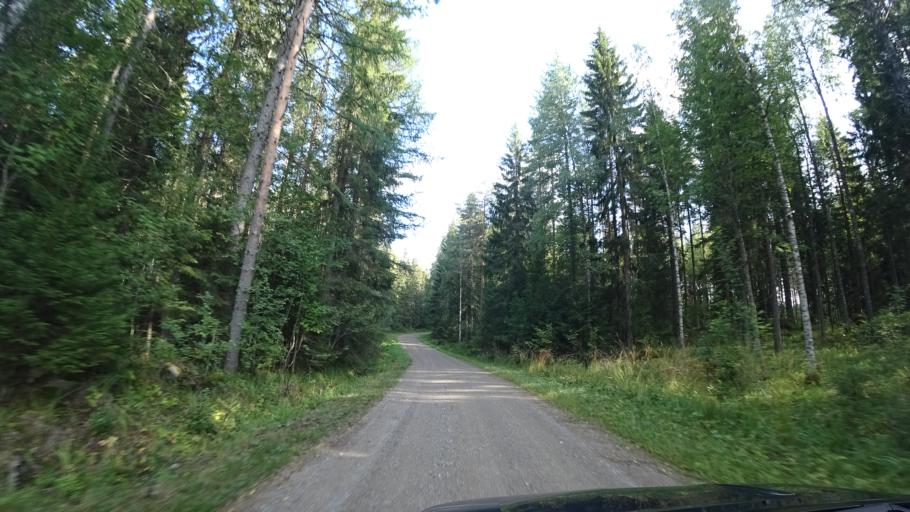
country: FI
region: Paijanne Tavastia
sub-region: Lahti
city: Auttoinen
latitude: 61.2195
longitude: 25.1493
